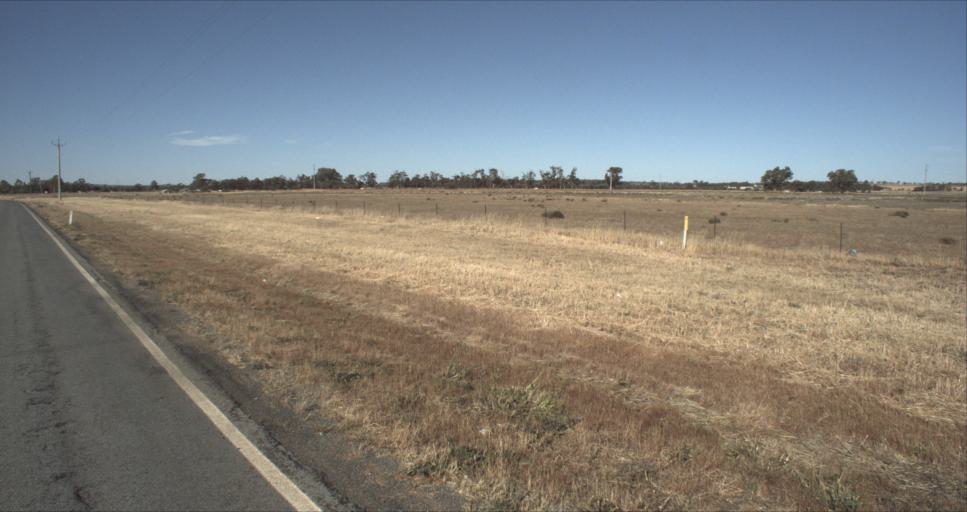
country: AU
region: New South Wales
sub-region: Leeton
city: Leeton
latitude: -34.6150
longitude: 146.4016
